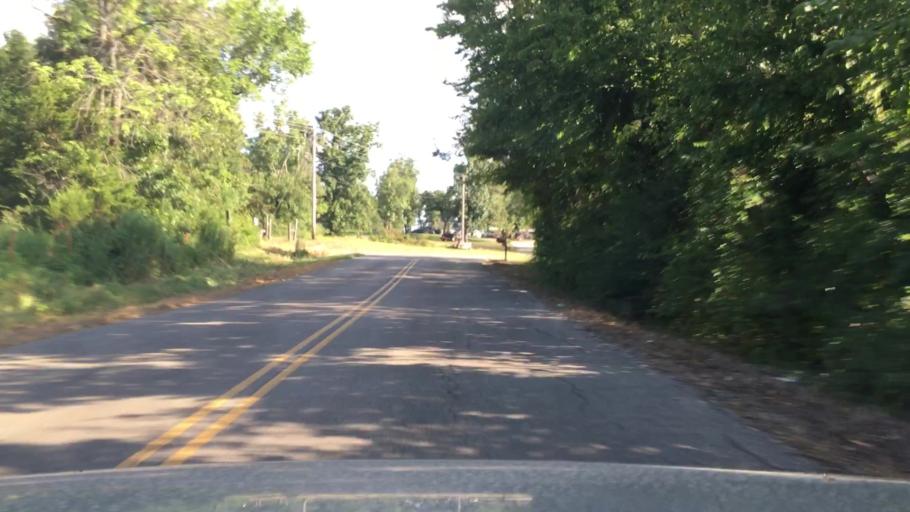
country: US
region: Oklahoma
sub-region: Muskogee County
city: Fort Gibson
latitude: 35.9103
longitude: -95.1587
